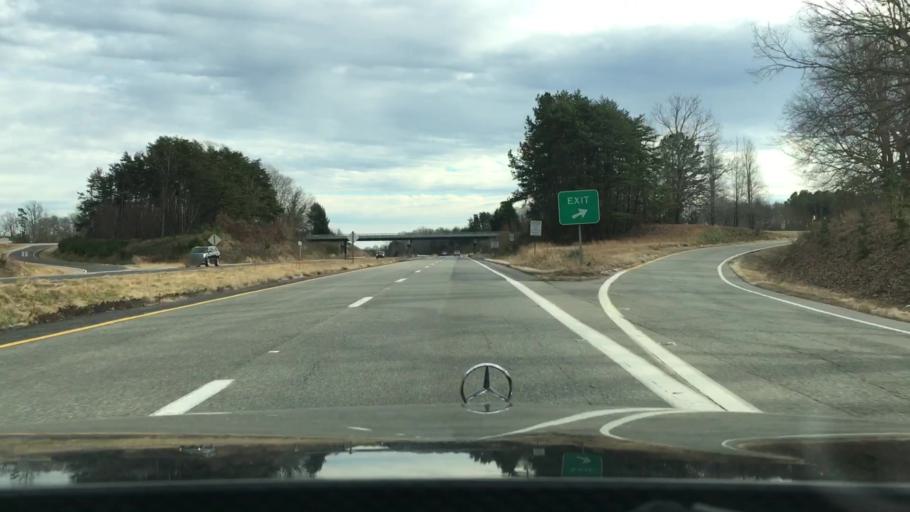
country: US
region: Virginia
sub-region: Pittsylvania County
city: Chatham
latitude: 36.8510
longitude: -79.3950
